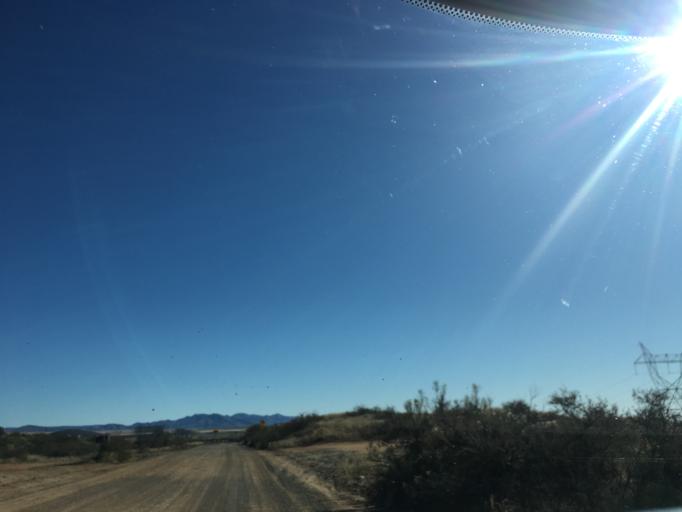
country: US
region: Arizona
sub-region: Yavapai County
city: Cordes Lakes
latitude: 34.2851
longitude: -112.1225
